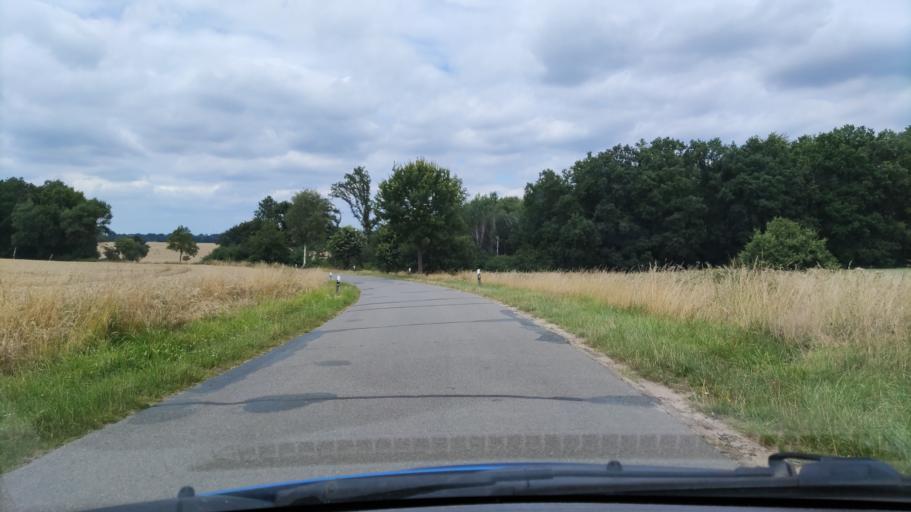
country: DE
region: Lower Saxony
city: Weste
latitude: 53.0697
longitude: 10.6925
